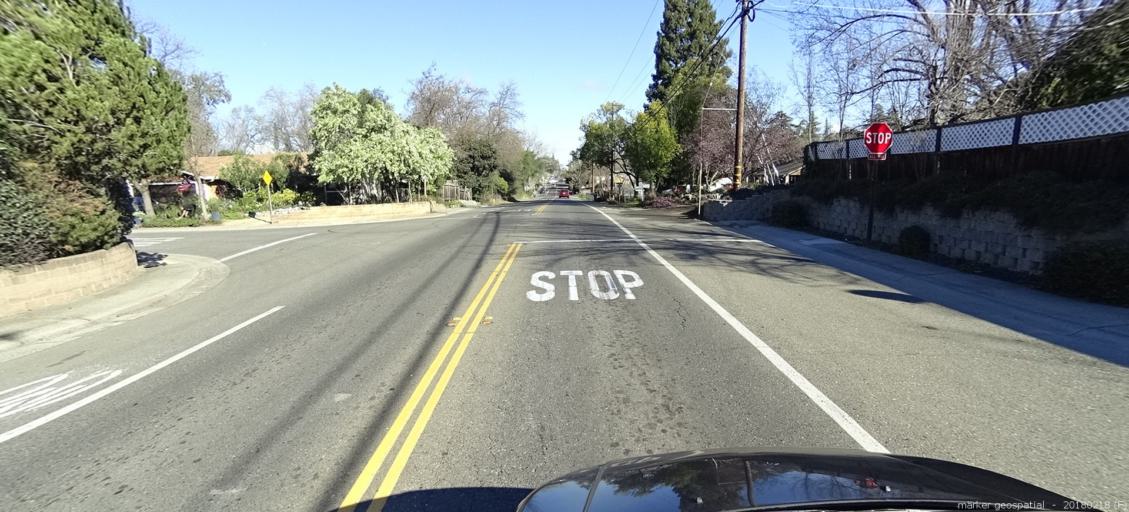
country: US
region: California
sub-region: Sacramento County
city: Orangevale
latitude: 38.6752
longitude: -121.2350
